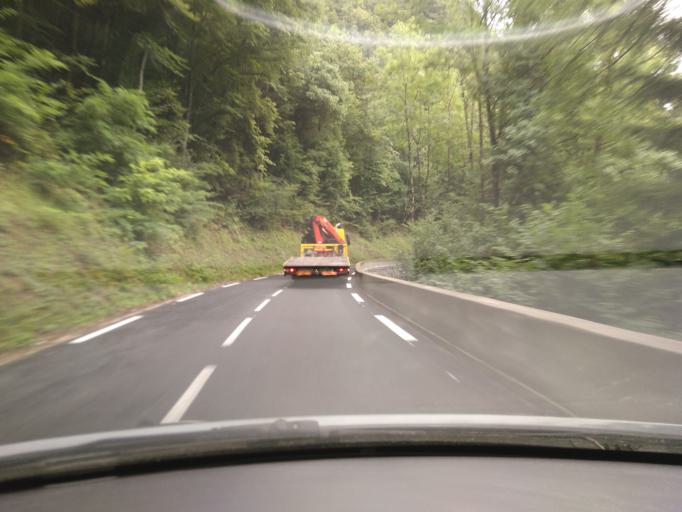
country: FR
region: Rhone-Alpes
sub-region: Departement de la Haute-Savoie
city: Bonneville
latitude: 46.0393
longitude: 6.3814
